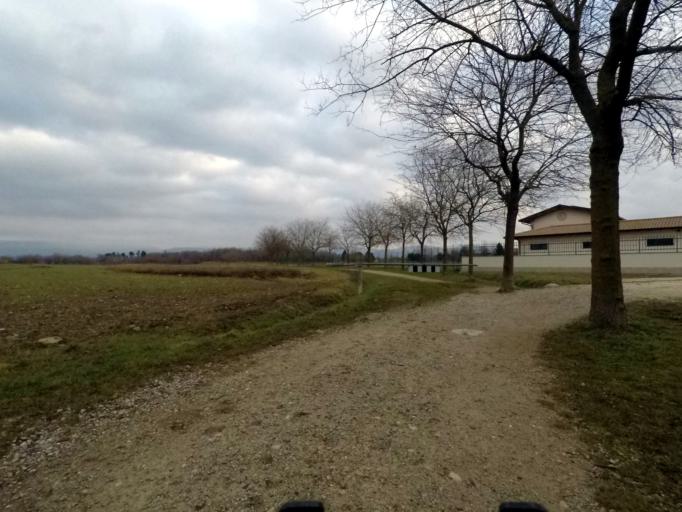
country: IT
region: Friuli Venezia Giulia
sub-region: Provincia di Udine
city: Colugna
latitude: 46.0955
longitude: 13.2005
